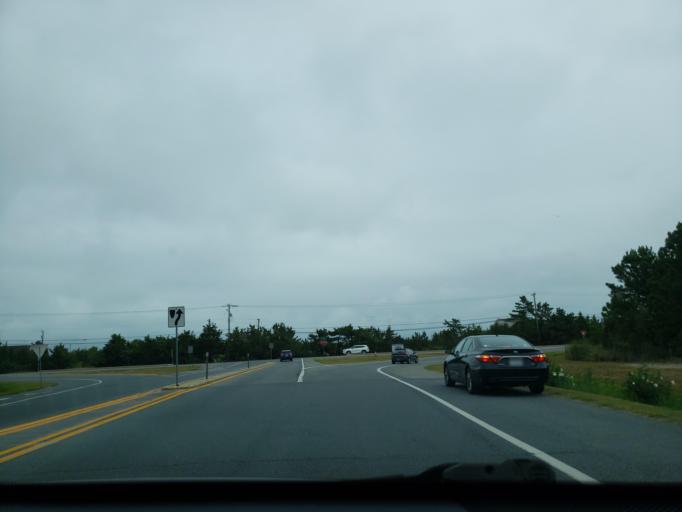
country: US
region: Delaware
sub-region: Sussex County
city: Lewes
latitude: 38.7794
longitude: -75.1265
